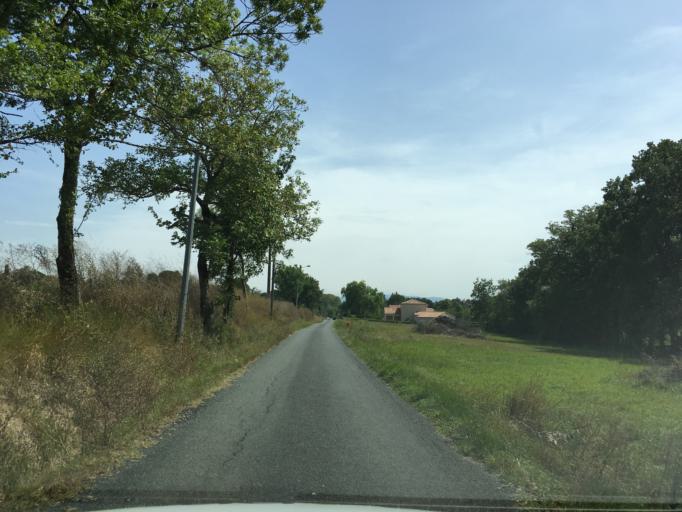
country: FR
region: Midi-Pyrenees
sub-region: Departement du Tarn
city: Castres
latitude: 43.6231
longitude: 2.2356
